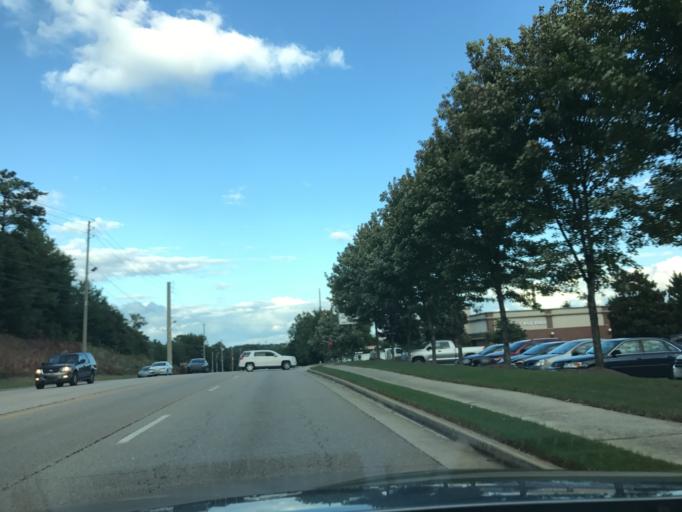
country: US
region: Georgia
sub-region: Douglas County
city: Douglasville
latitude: 33.7287
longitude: -84.7531
